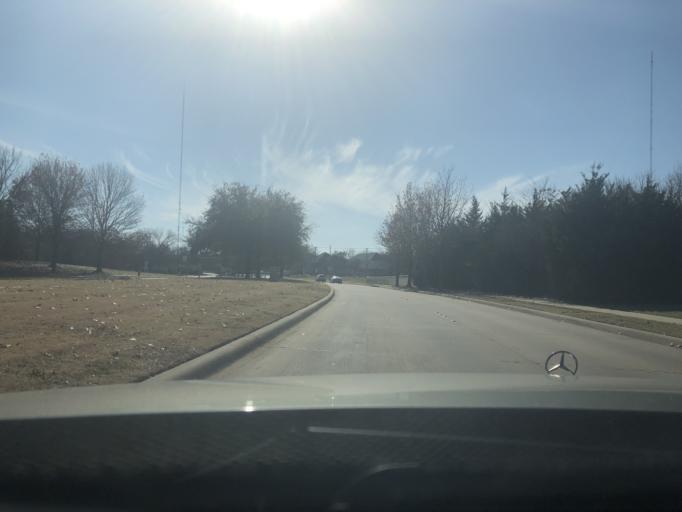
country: US
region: Texas
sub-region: Dallas County
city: Cedar Hill
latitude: 32.5918
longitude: -96.9518
